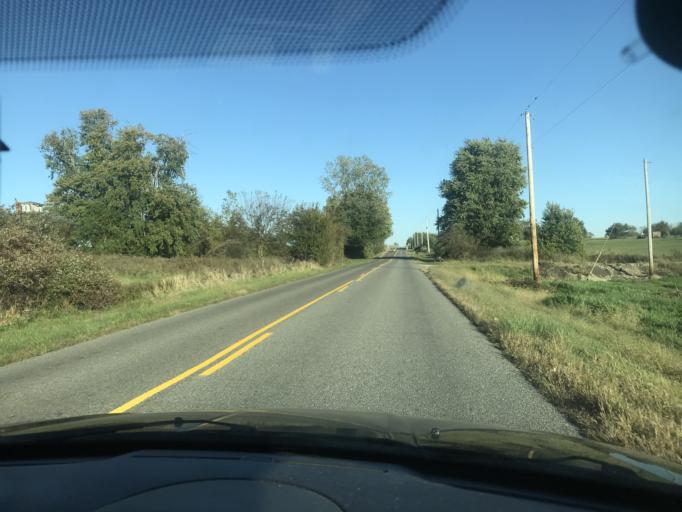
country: US
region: Ohio
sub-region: Logan County
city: De Graff
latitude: 40.3221
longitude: -83.8394
